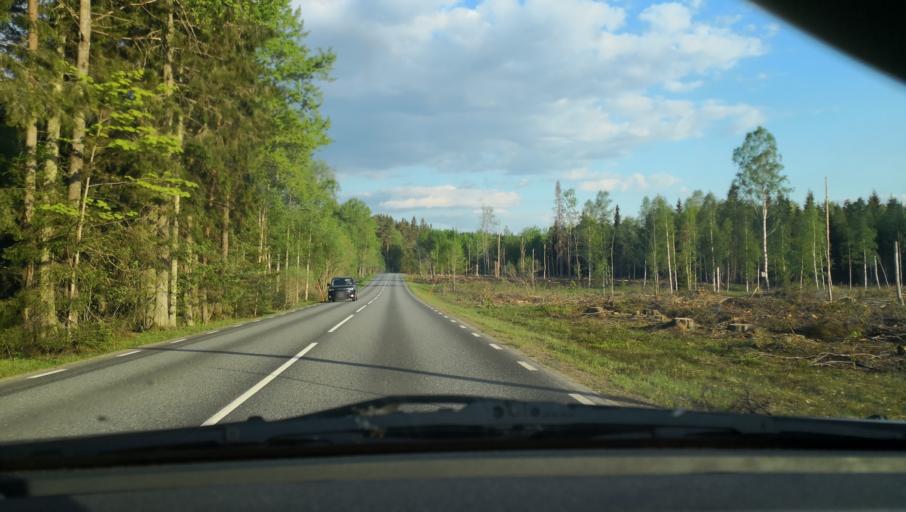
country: SE
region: Joenkoeping
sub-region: Vetlanda Kommun
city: Landsbro
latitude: 57.3875
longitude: 14.8367
